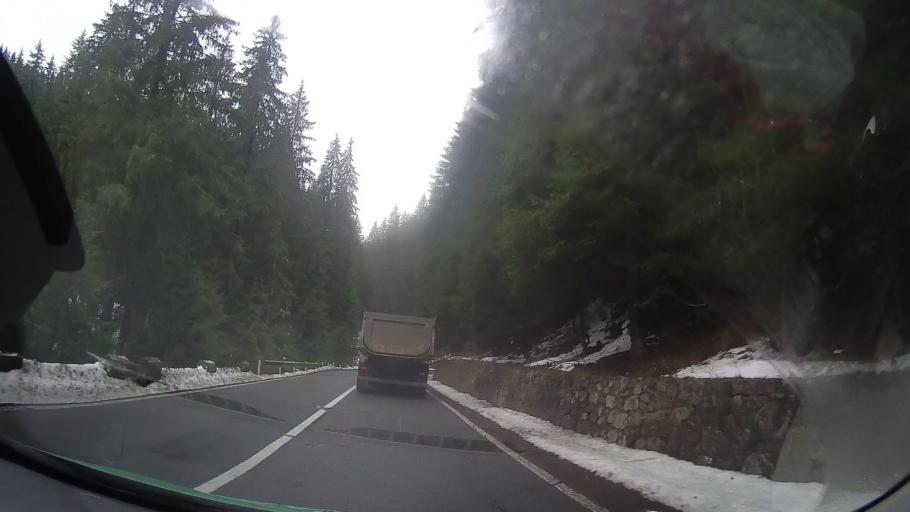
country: RO
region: Harghita
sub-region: Oras Balan
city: Balan
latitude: 46.7758
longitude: 25.7410
